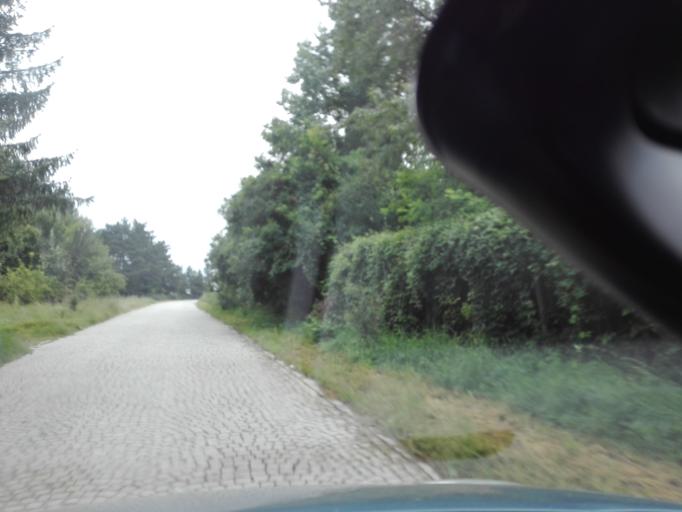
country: BG
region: Sofia-Capital
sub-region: Stolichna Obshtina
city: Sofia
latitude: 42.6046
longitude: 23.3985
